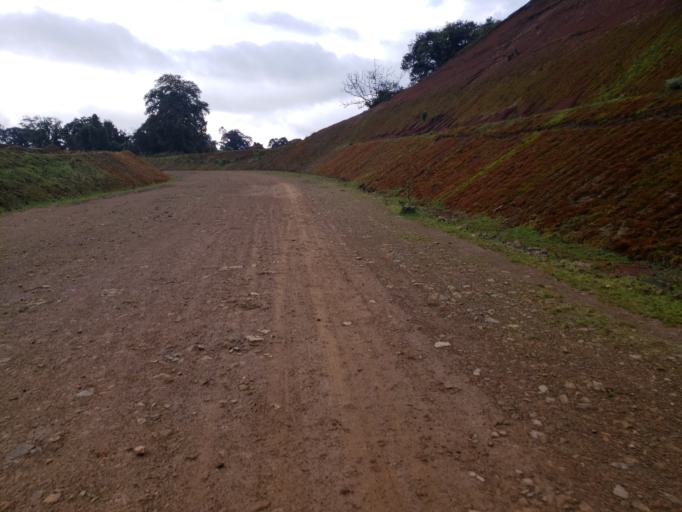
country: ET
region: Oromiya
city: Dodola
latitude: 6.6703
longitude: 39.3642
